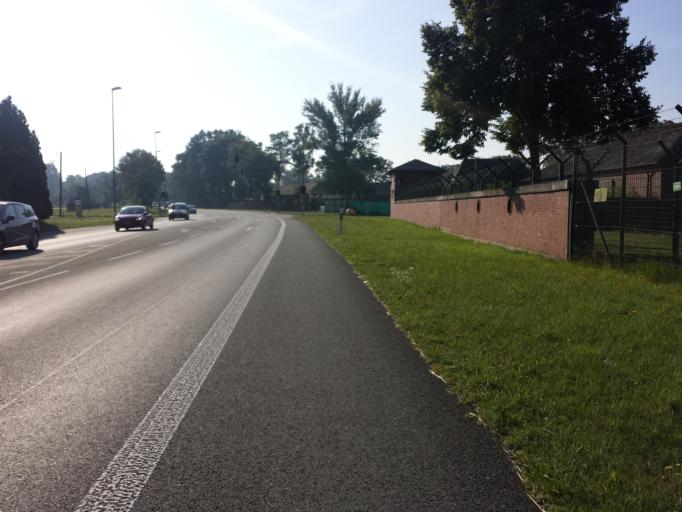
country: DE
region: North Rhine-Westphalia
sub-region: Regierungsbezirk Detmold
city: Guetersloh
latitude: 51.9287
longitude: 8.3173
